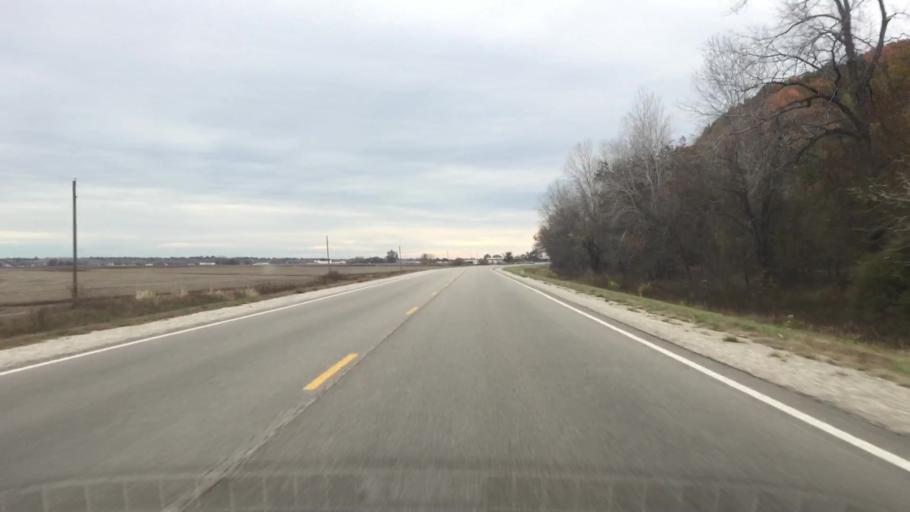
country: US
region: Missouri
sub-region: Cole County
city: Jefferson City
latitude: 38.5867
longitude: -92.1224
